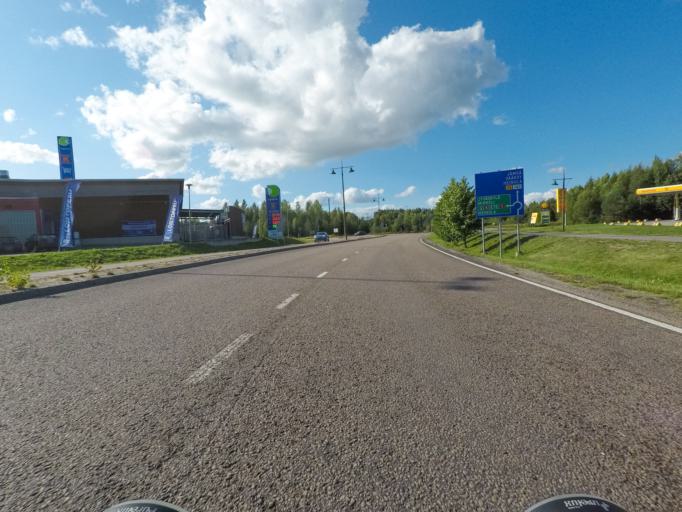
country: FI
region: Paijanne Tavastia
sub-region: Lahti
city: Lahti
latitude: 60.9834
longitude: 25.7386
